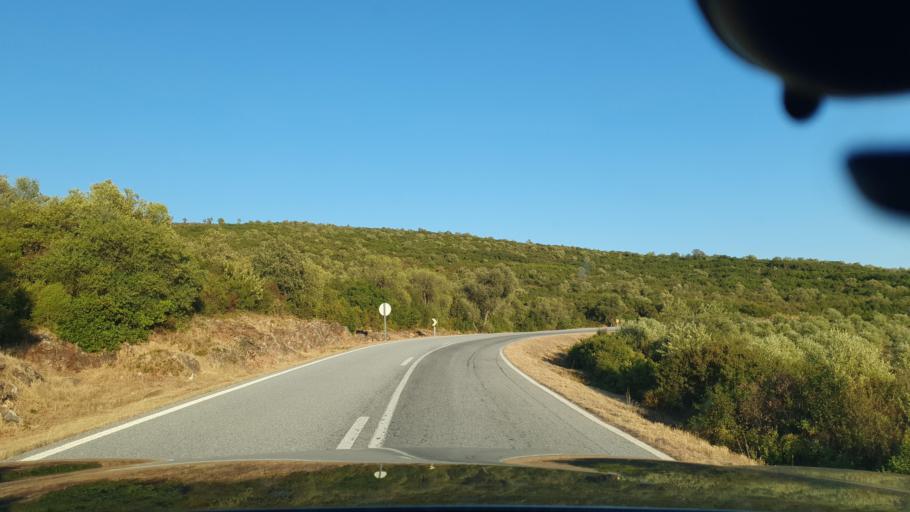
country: PT
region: Evora
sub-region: Estremoz
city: Estremoz
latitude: 38.9197
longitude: -7.6647
